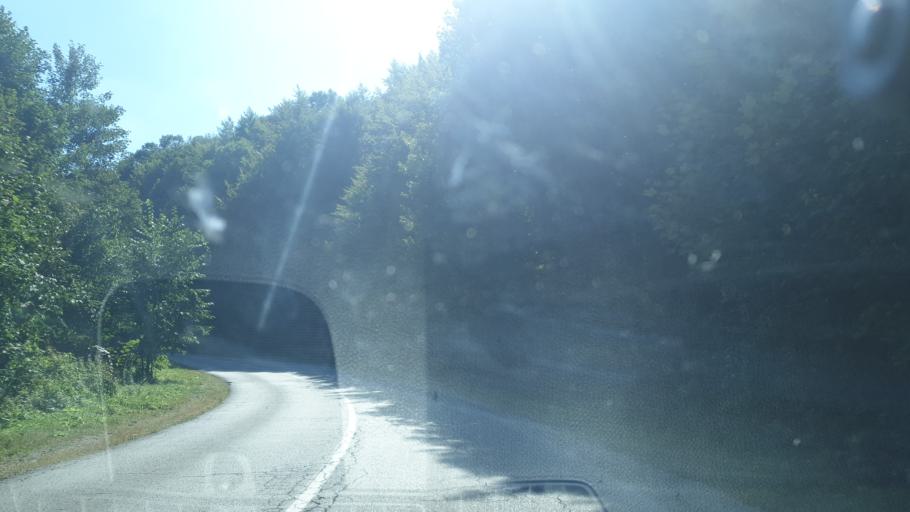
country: RS
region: Central Serbia
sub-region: Kolubarski Okrug
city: Mionica
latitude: 44.1376
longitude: 20.0179
